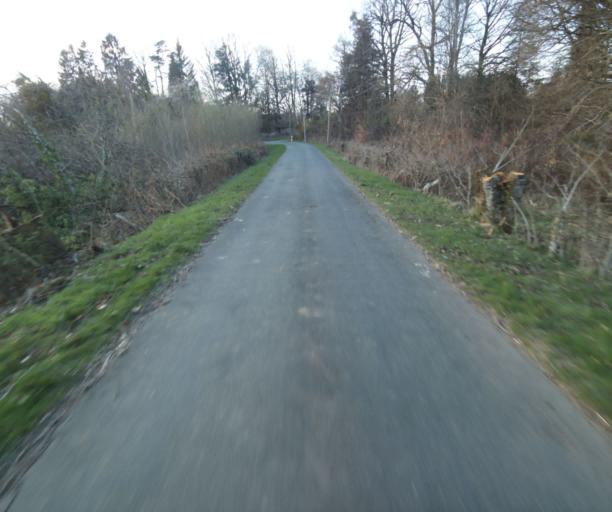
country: FR
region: Limousin
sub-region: Departement de la Correze
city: Uzerche
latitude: 45.3691
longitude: 1.5865
